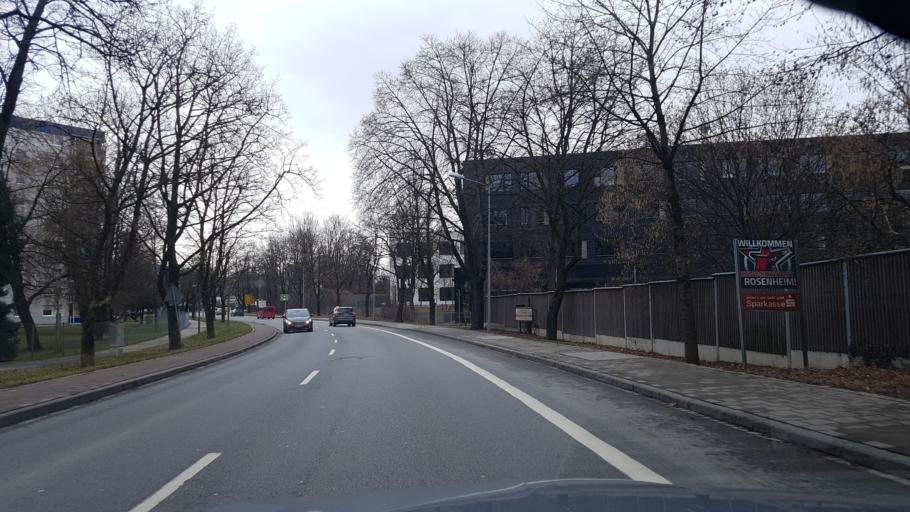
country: DE
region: Bavaria
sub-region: Upper Bavaria
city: Rosenheim
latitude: 47.8640
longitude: 12.1099
